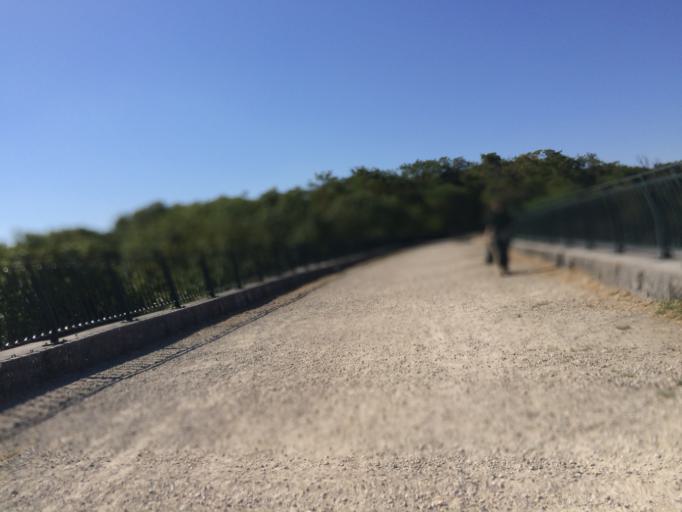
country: FR
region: Ile-de-France
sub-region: Departement de l'Essonne
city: Gometz-le-Chatel
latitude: 48.6789
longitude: 2.1526
